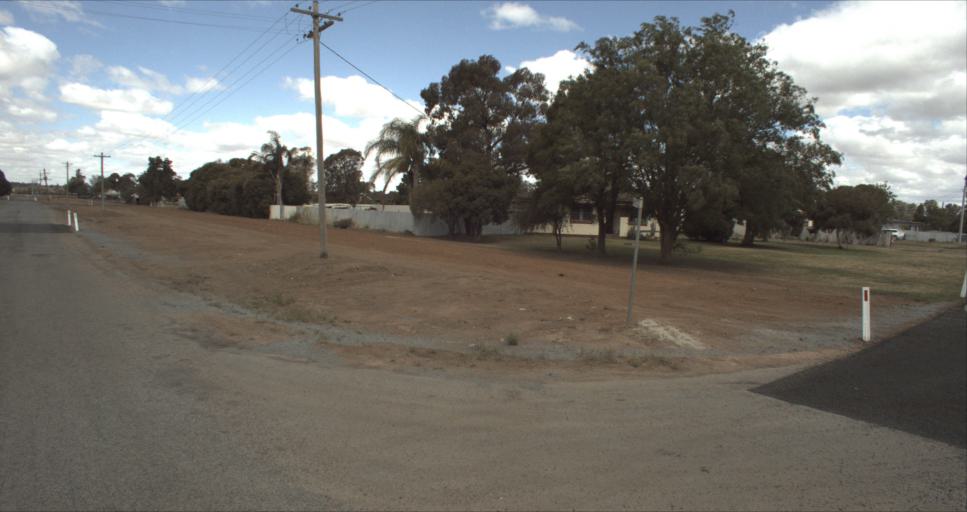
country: AU
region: New South Wales
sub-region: Leeton
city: Leeton
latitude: -34.5939
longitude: 146.4086
